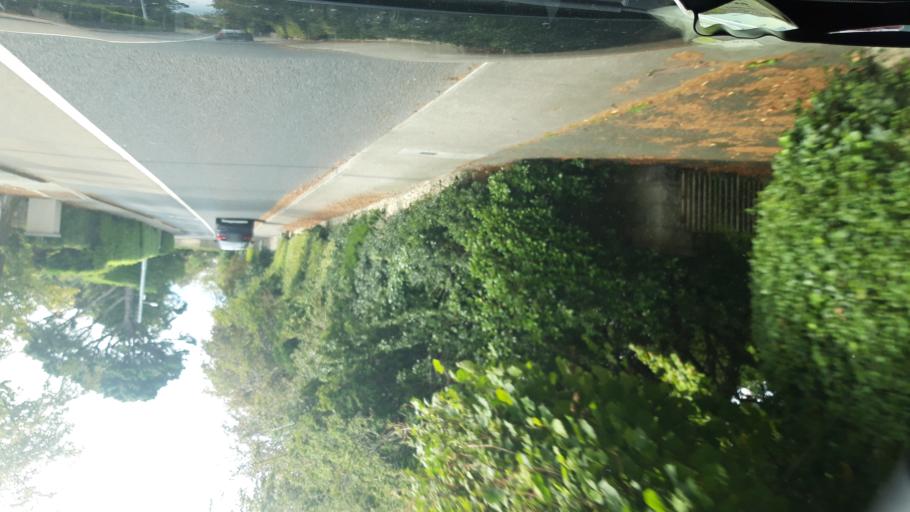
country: IE
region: Leinster
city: Foxrock
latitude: 53.2736
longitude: -6.1912
